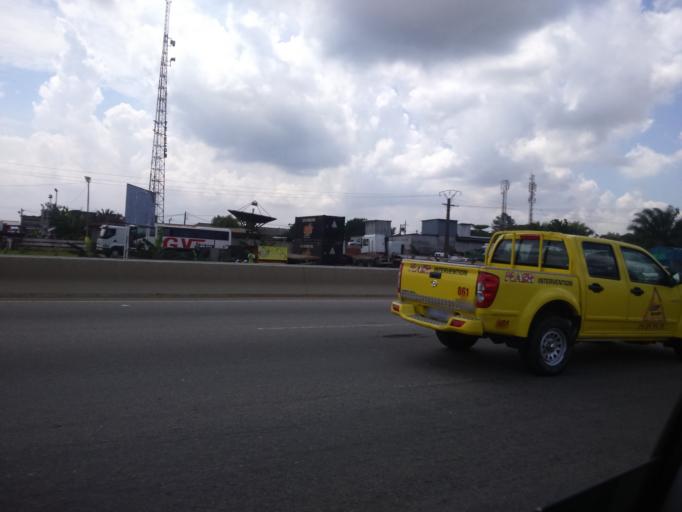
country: CI
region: Lagunes
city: Abobo
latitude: 5.3630
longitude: -4.0819
